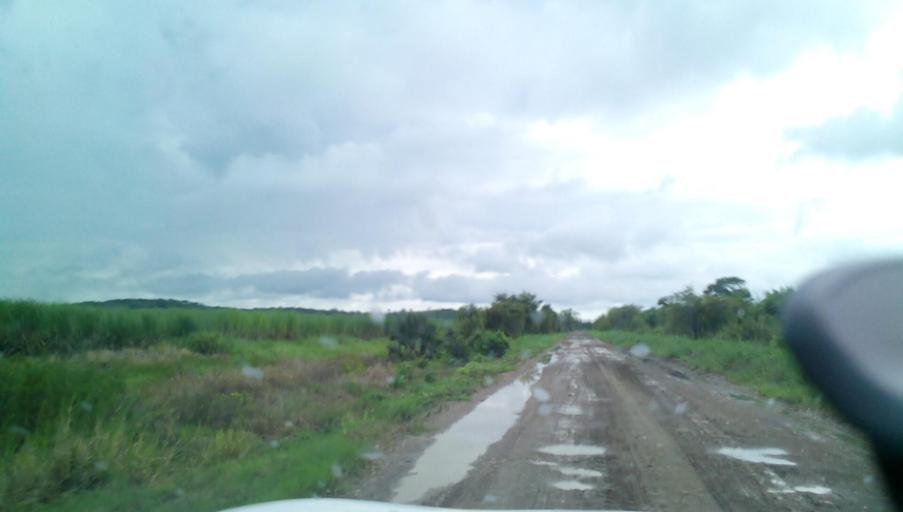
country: MX
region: Veracruz
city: Panuco
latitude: 21.8237
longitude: -98.1108
